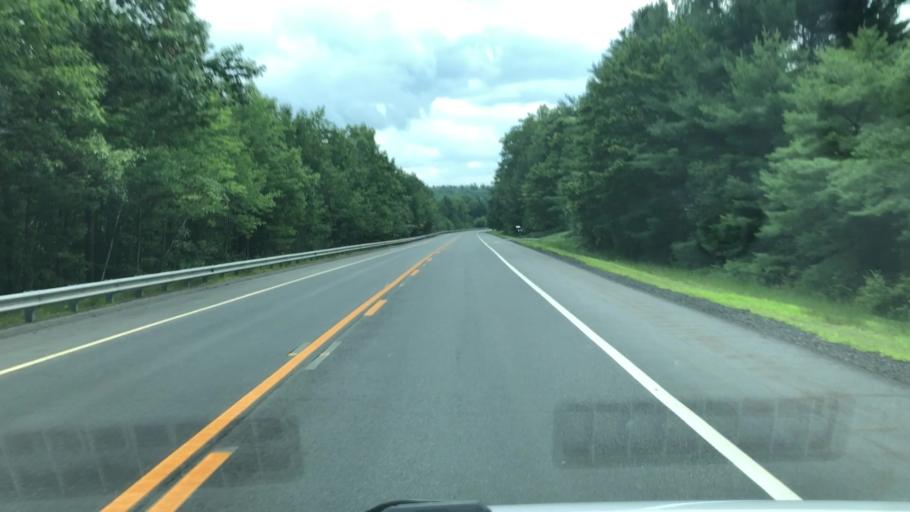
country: US
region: Massachusetts
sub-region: Franklin County
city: Ashfield
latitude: 42.4988
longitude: -72.8079
